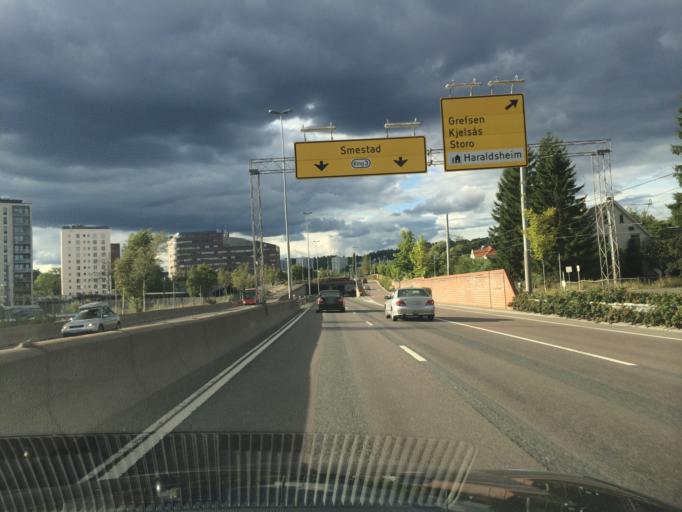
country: NO
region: Oslo
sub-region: Oslo
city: Oslo
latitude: 59.9427
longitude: 10.7807
